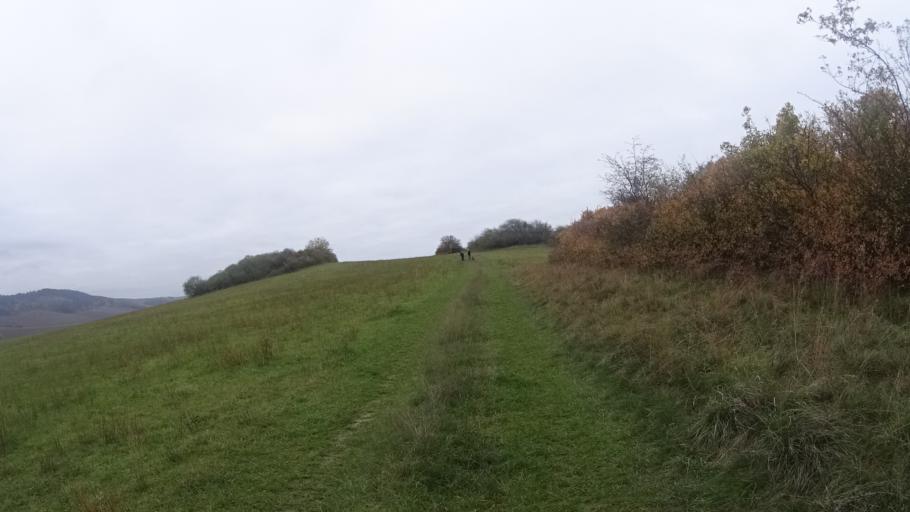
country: DE
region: Thuringia
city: Arnstadt
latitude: 50.8489
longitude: 10.9254
